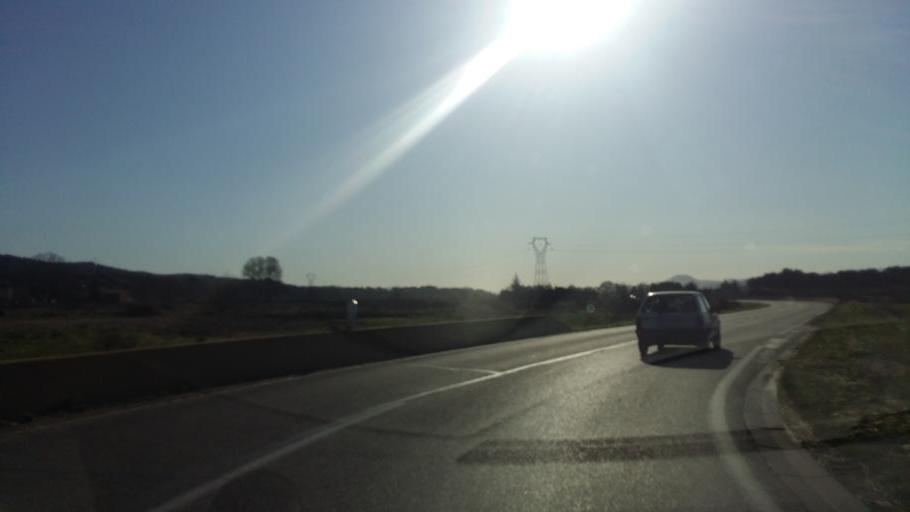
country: FR
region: Provence-Alpes-Cote d'Azur
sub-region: Departement du Vaucluse
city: Villelaure
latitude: 43.7071
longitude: 5.4380
